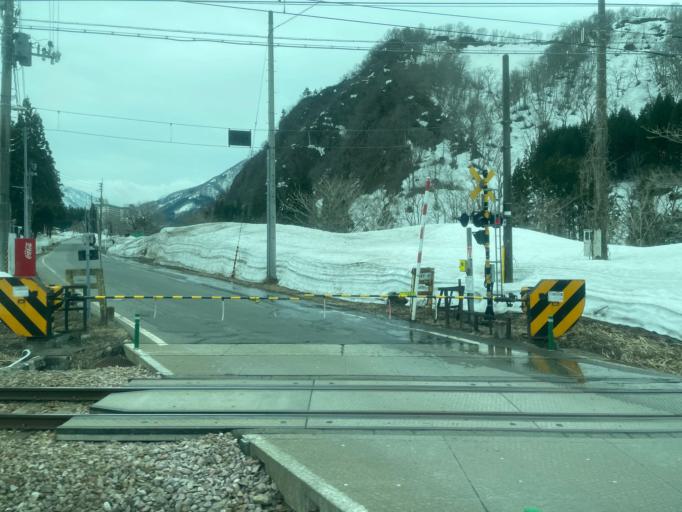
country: JP
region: Niigata
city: Shiozawa
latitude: 36.9245
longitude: 138.8368
